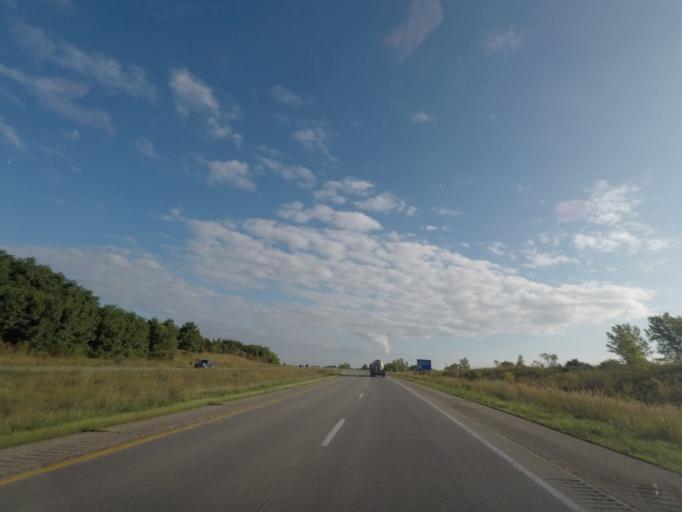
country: US
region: Iowa
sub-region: Polk County
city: Pleasant Hill
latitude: 41.5883
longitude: -93.5006
